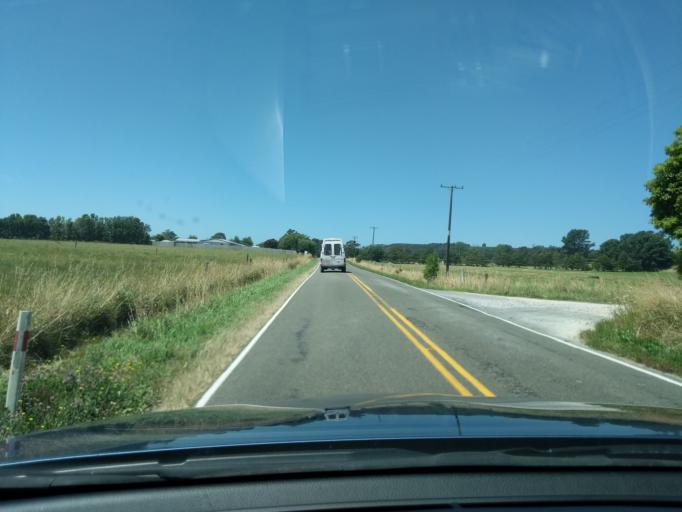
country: NZ
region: Tasman
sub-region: Tasman District
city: Takaka
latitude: -40.6860
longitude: 172.6538
